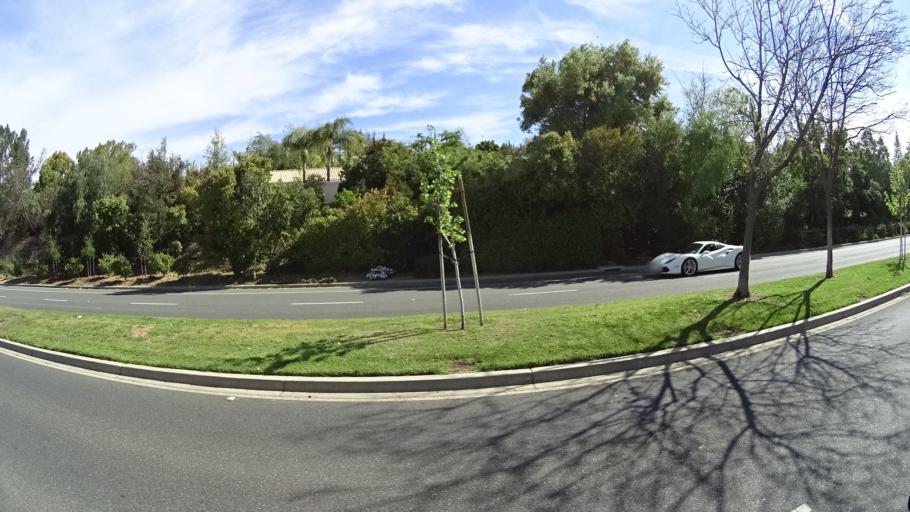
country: US
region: California
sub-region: Ventura County
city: Thousand Oaks
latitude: 34.1977
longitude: -118.8109
